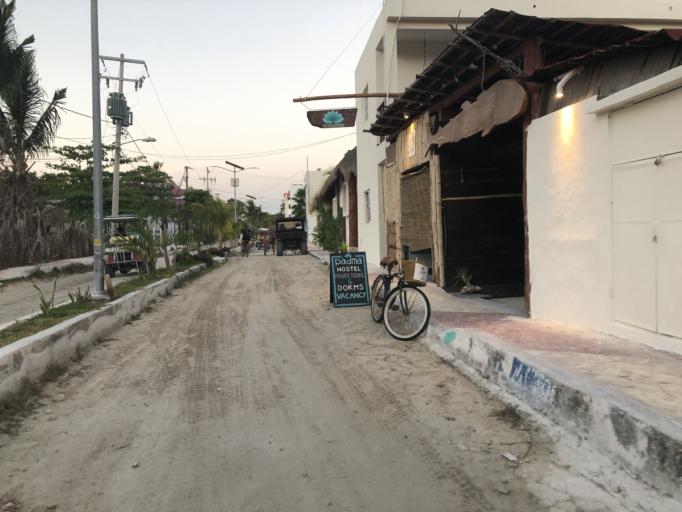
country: MX
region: Quintana Roo
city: Kantunilkin
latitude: 21.5232
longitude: -87.3811
